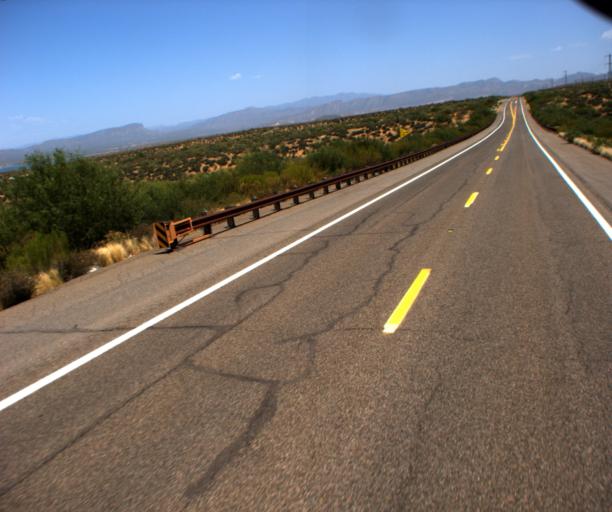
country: US
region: Arizona
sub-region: Gila County
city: Tonto Basin
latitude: 33.6512
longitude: -111.1005
